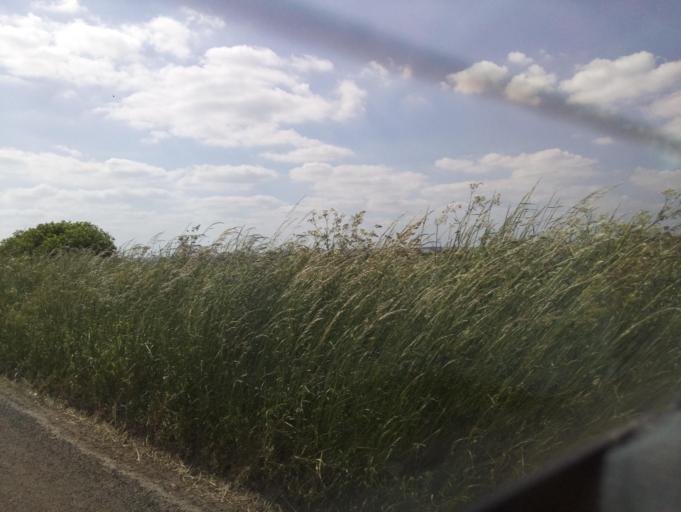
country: GB
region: England
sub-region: Wiltshire
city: Milston
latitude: 51.2521
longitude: -1.7555
